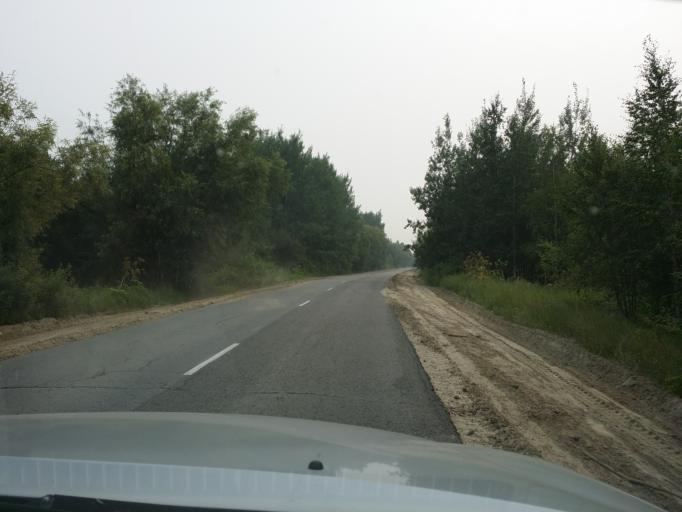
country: RU
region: Khanty-Mansiyskiy Avtonomnyy Okrug
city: Megion
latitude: 60.9815
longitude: 76.2974
